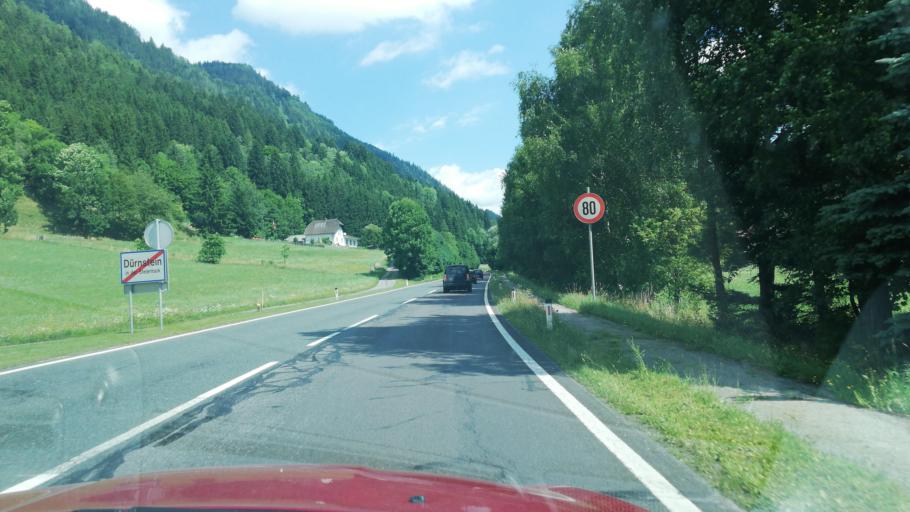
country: AT
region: Styria
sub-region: Politischer Bezirk Murau
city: Durnstein in der Steiermark
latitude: 46.9985
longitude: 14.3921
